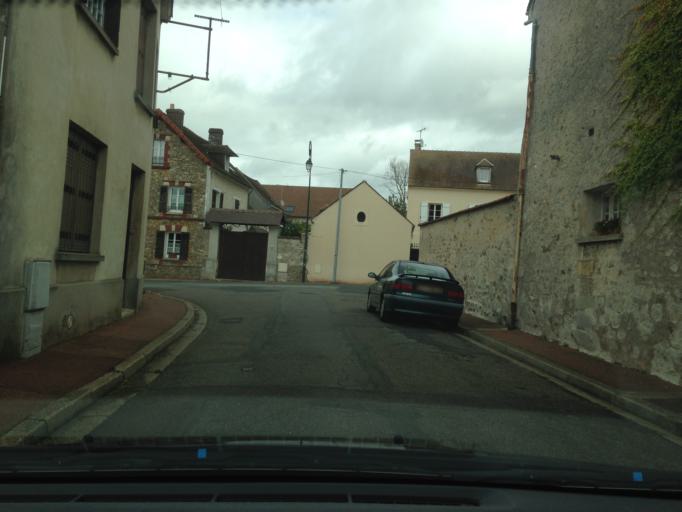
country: FR
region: Ile-de-France
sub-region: Departement du Val-d'Oise
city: Marines
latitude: 49.1315
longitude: 2.0505
